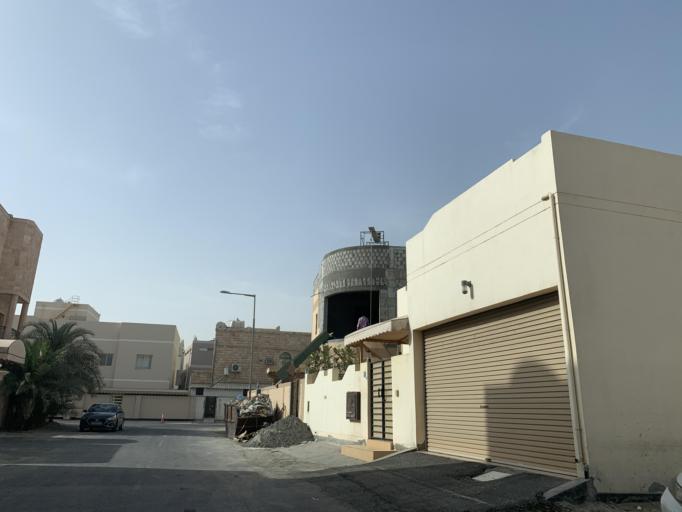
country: BH
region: Northern
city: Madinat `Isa
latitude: 26.1807
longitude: 50.5645
